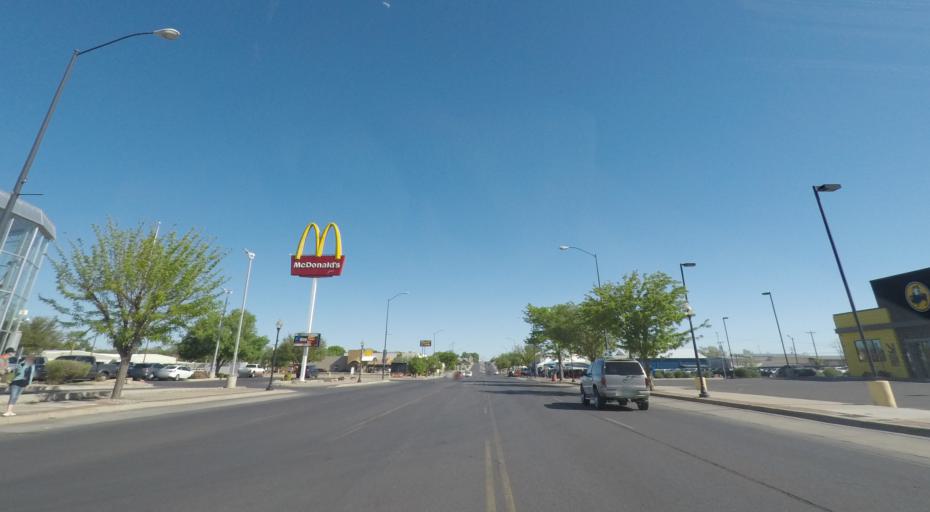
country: US
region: New Mexico
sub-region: Chaves County
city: Roswell
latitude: 33.4003
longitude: -104.5228
